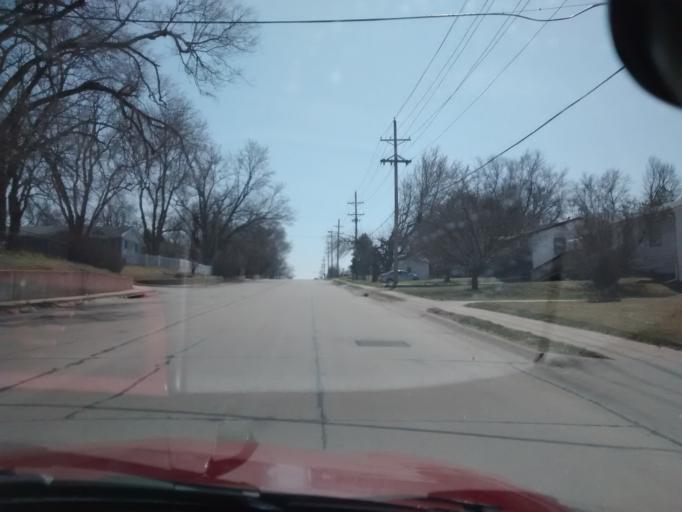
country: US
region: Nebraska
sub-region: Sarpy County
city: Bellevue
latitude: 41.1450
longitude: -95.9075
